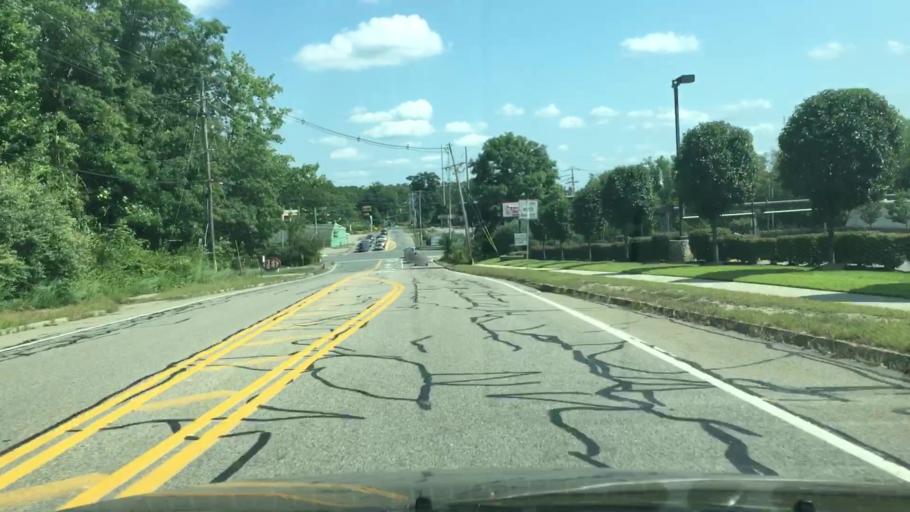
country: US
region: Massachusetts
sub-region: Worcester County
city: Milford
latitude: 42.1541
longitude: -71.4914
